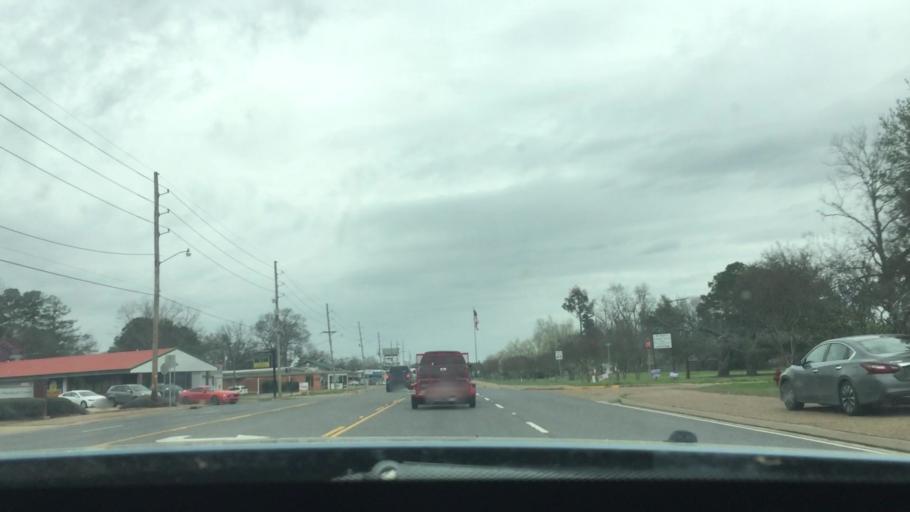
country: US
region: Louisiana
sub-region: Franklin Parish
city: Winnsboro
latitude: 32.1593
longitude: -91.7170
